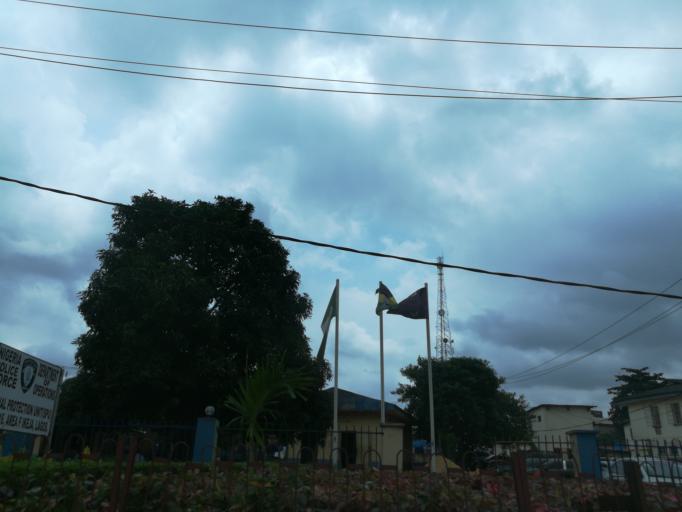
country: NG
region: Lagos
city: Ikeja
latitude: 6.5899
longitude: 3.3453
